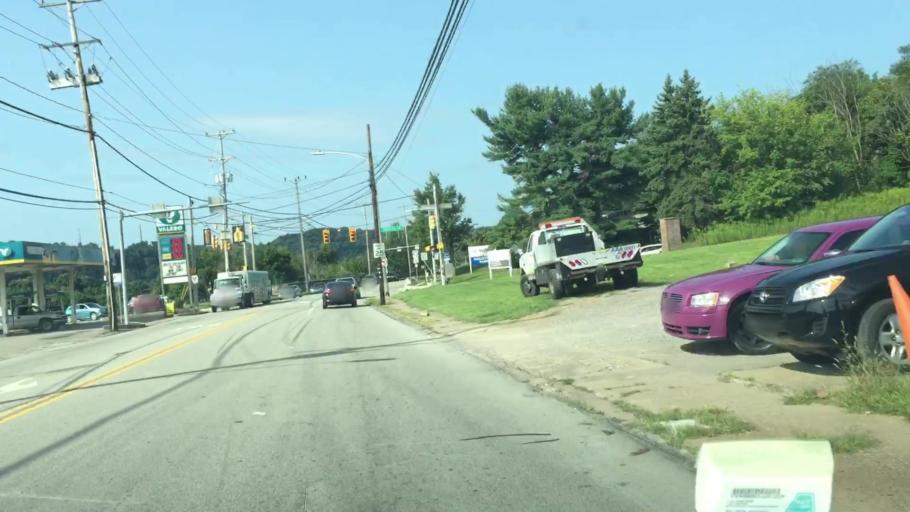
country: US
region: Pennsylvania
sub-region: Allegheny County
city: Blawnox
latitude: 40.4919
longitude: -79.8652
